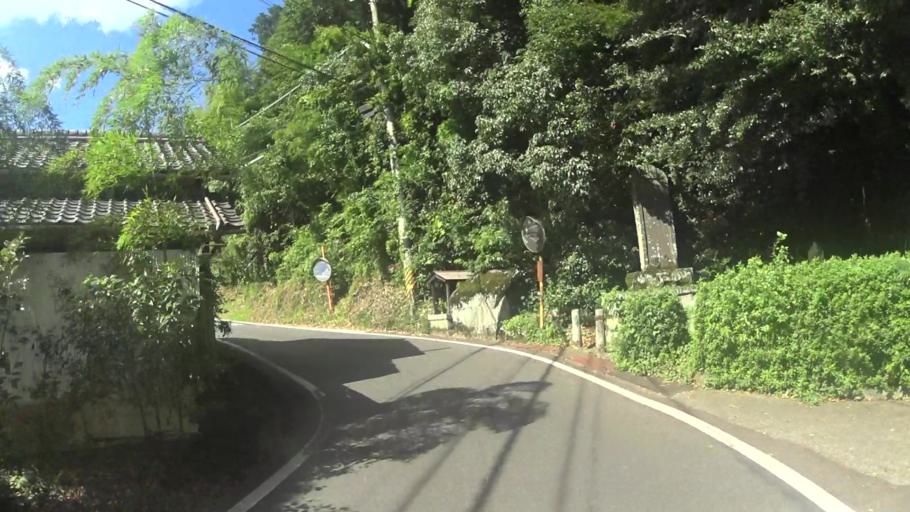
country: JP
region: Mie
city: Ueno-ebisumachi
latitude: 34.7393
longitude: 136.0217
